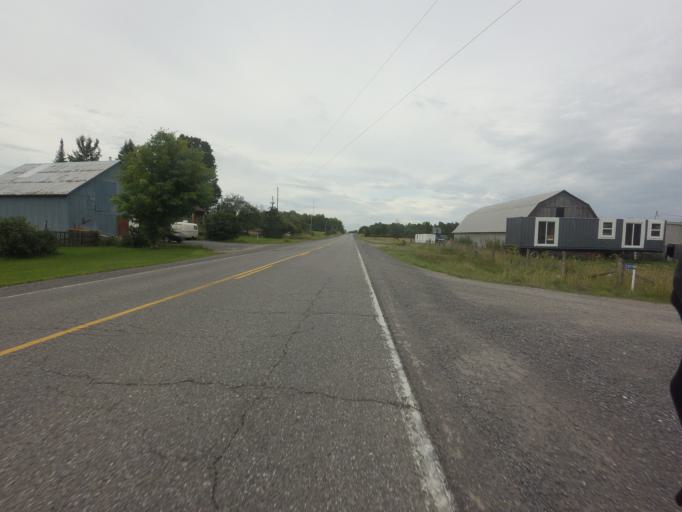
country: CA
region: Ontario
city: Carleton Place
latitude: 45.1579
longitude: -76.2978
